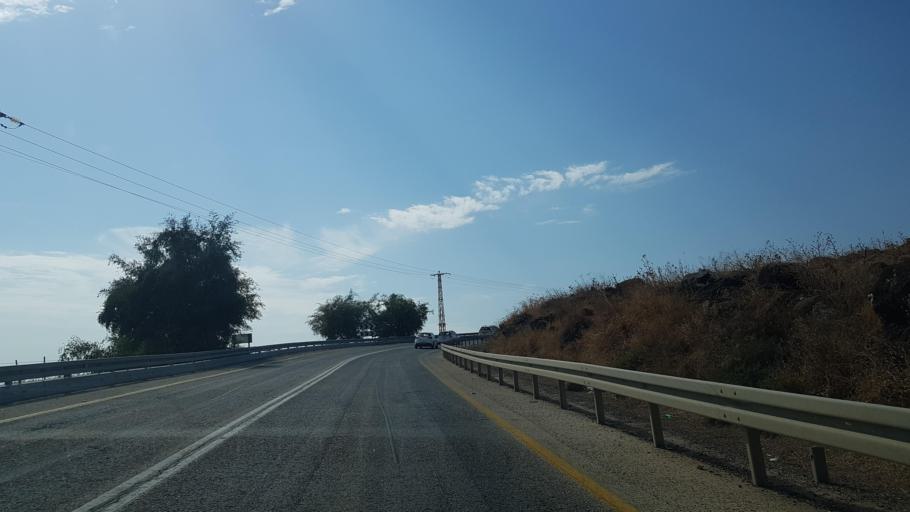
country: SY
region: Quneitra
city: Al Butayhah
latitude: 32.9106
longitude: 35.5831
